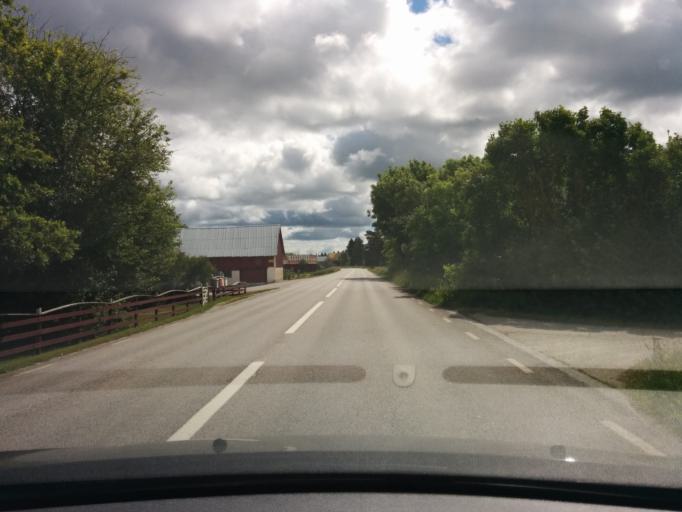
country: SE
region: Gotland
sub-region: Gotland
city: Slite
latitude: 57.6293
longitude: 18.5723
